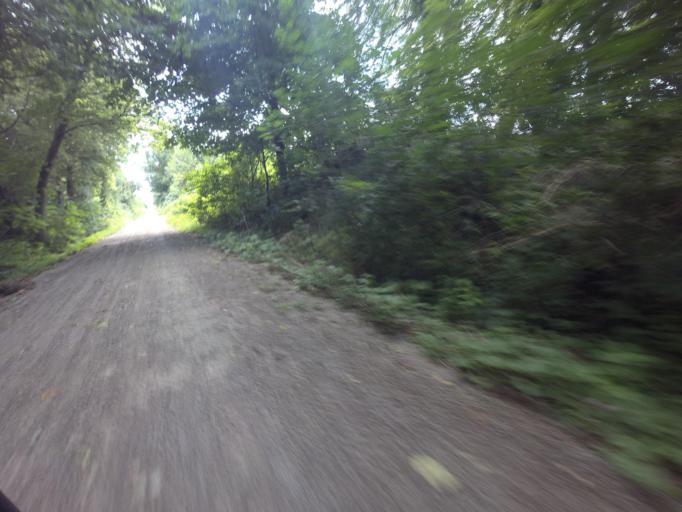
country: CA
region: Ontario
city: Huron East
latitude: 43.6230
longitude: -81.1608
